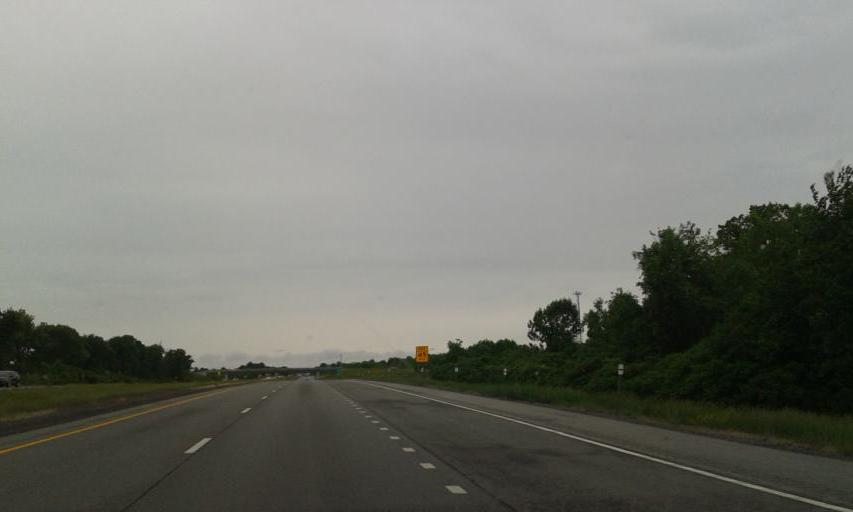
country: US
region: New York
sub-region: Genesee County
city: Le Roy
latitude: 43.0290
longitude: -77.9583
